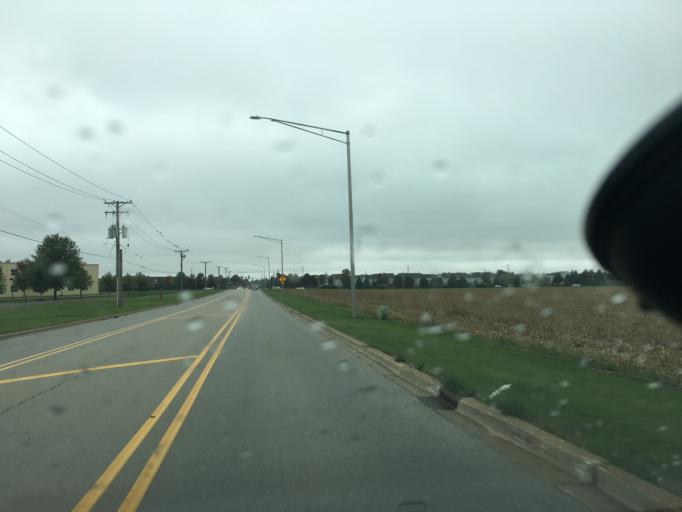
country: US
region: Illinois
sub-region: Will County
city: Plainfield
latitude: 41.6660
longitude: -88.2193
